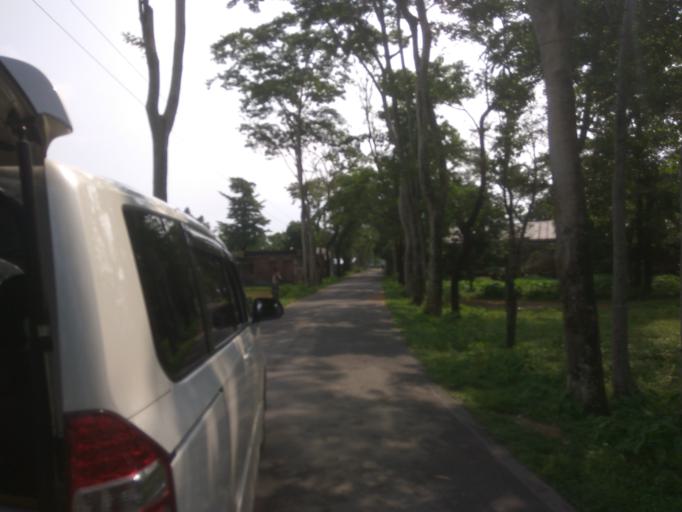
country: IN
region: Assam
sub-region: Karimganj
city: Karimganj
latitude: 24.8238
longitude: 92.2258
